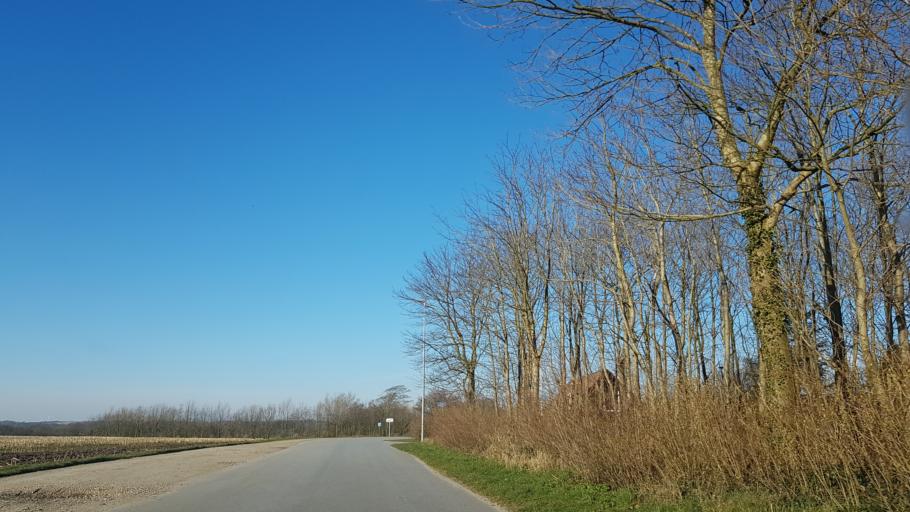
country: DK
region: South Denmark
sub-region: Vejen Kommune
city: Brorup
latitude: 55.4108
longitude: 8.9703
